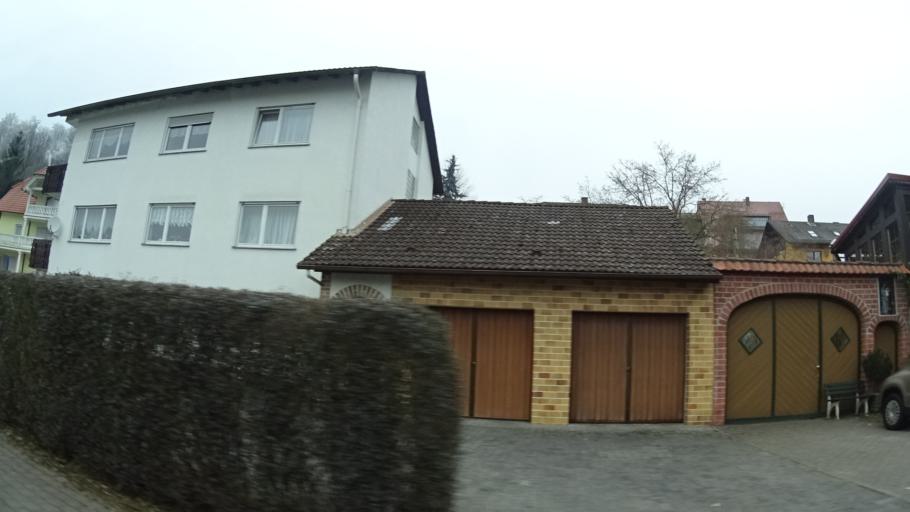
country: DE
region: Bavaria
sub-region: Regierungsbezirk Unterfranken
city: Bad Bruckenau
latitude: 50.3203
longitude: 9.8165
